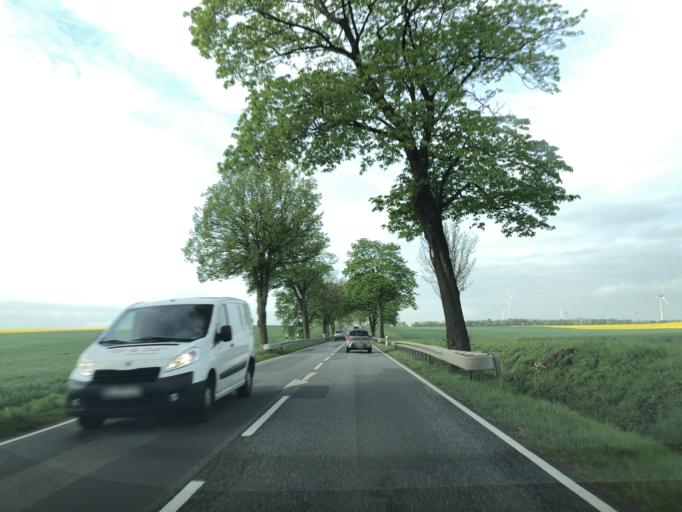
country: DE
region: Mecklenburg-Vorpommern
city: Laage
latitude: 53.8811
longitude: 12.2459
